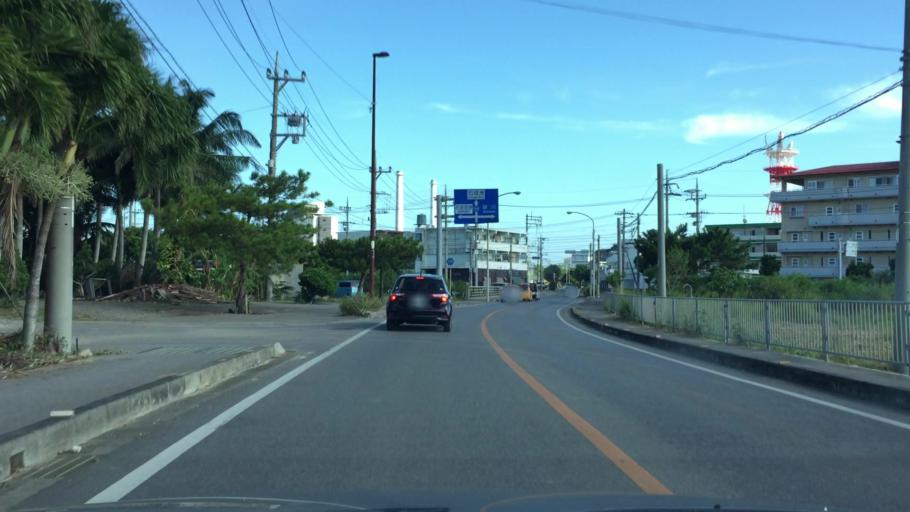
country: JP
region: Okinawa
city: Ishigaki
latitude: 24.3524
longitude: 124.1580
